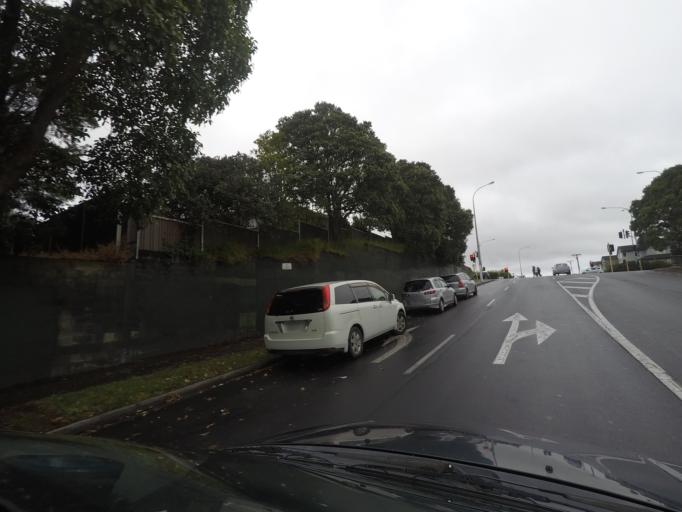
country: NZ
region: Auckland
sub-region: Auckland
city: Auckland
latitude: -36.8838
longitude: 174.7356
